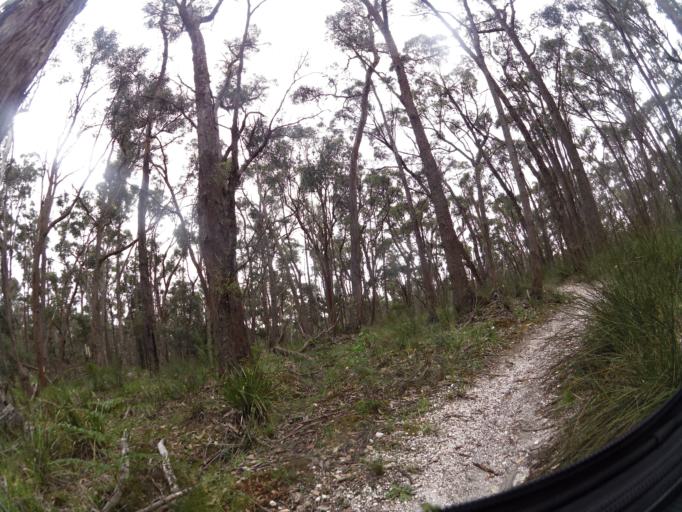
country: AU
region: Victoria
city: Brown Hill
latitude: -37.4594
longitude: 143.9084
